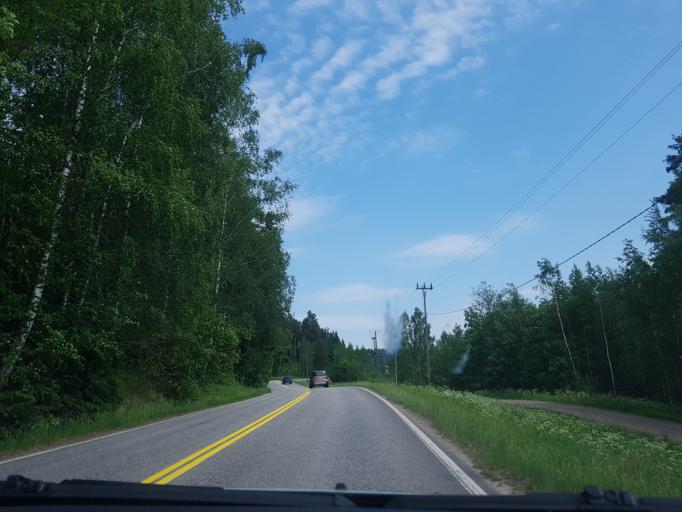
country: FI
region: Uusimaa
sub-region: Helsinki
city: Vihti
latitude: 60.3115
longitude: 24.4031
